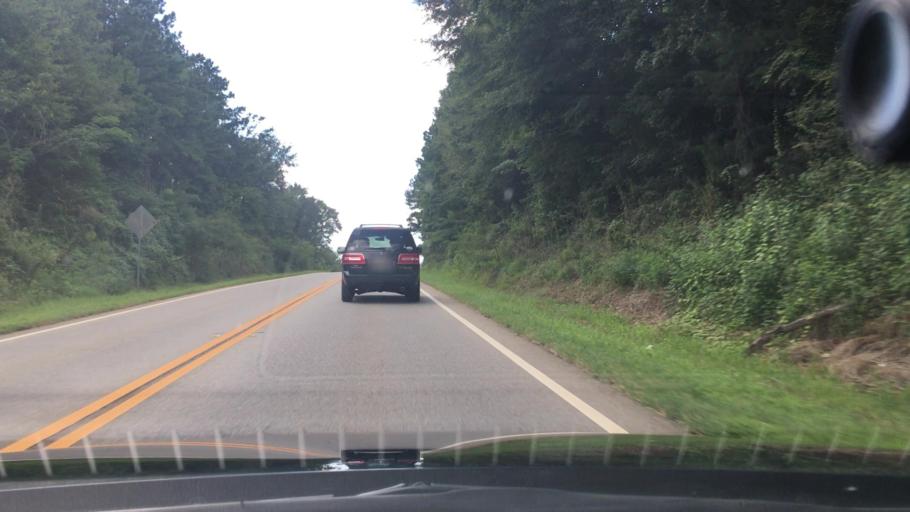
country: US
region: Georgia
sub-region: Putnam County
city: Eatonton
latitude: 33.3122
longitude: -83.4464
